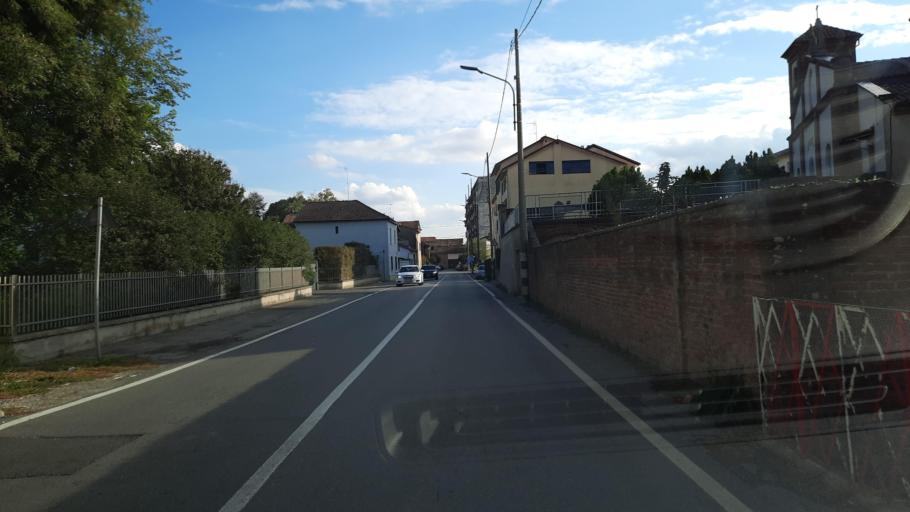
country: IT
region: Piedmont
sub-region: Provincia di Vercelli
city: Trino
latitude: 45.1988
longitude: 8.2935
